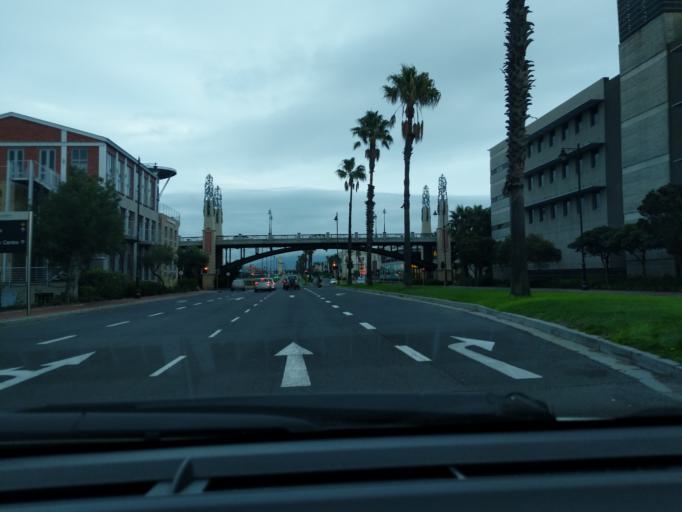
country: ZA
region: Western Cape
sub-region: City of Cape Town
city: Sunset Beach
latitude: -33.8913
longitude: 18.5168
